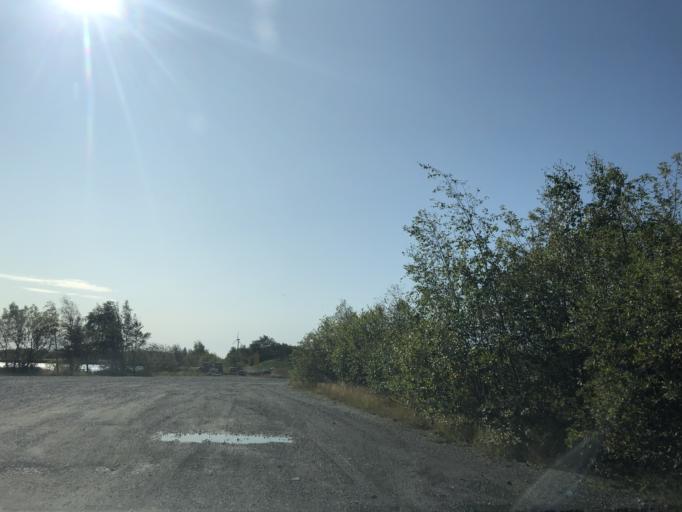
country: SE
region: Vaestra Goetaland
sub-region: Goteborg
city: Torslanda
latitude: 57.7097
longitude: 11.8046
